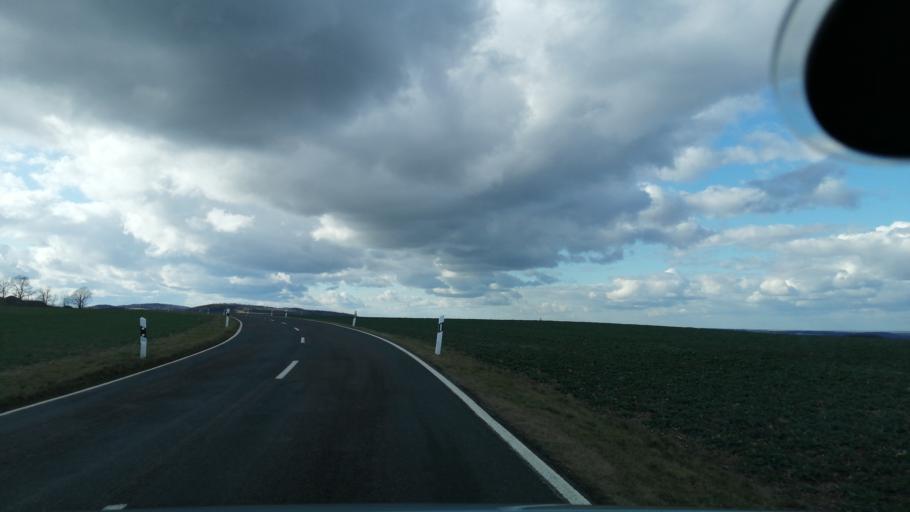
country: DE
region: Saxony
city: Hochkirch
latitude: 51.1453
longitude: 14.5588
